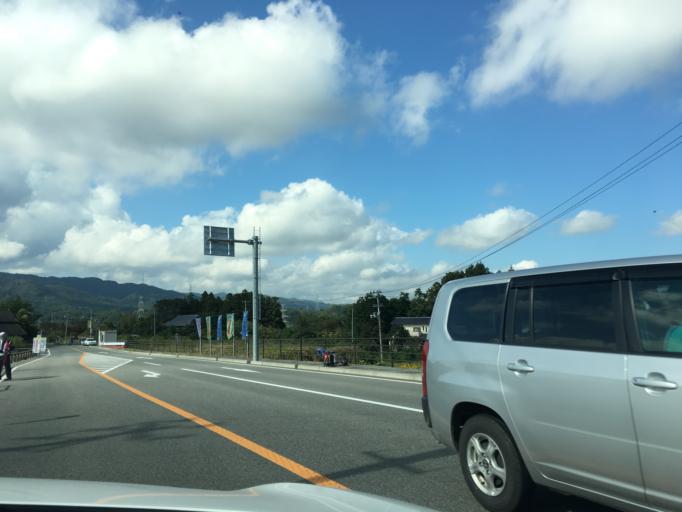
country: JP
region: Fukushima
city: Namie
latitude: 37.5017
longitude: 140.9471
